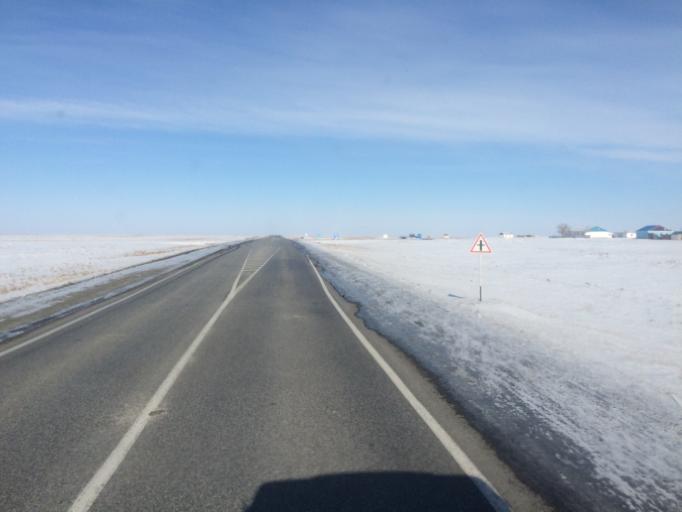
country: KZ
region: Qyzylorda
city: Sekseuil
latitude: 47.4780
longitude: 61.5359
